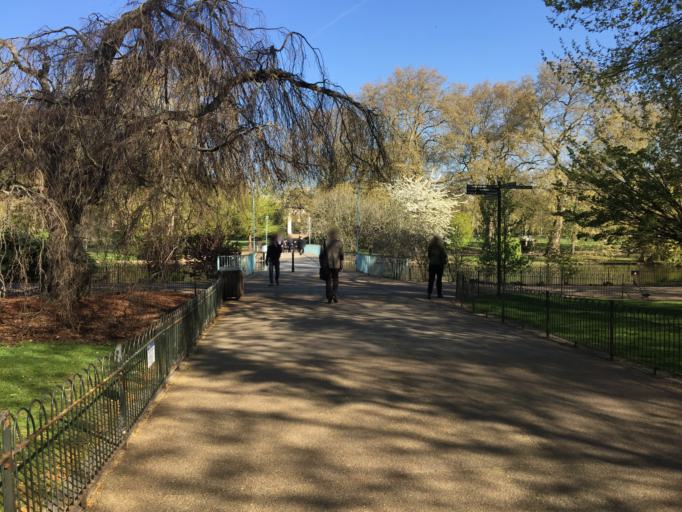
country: GB
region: England
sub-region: Greater London
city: London
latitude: 51.5019
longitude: -0.1350
